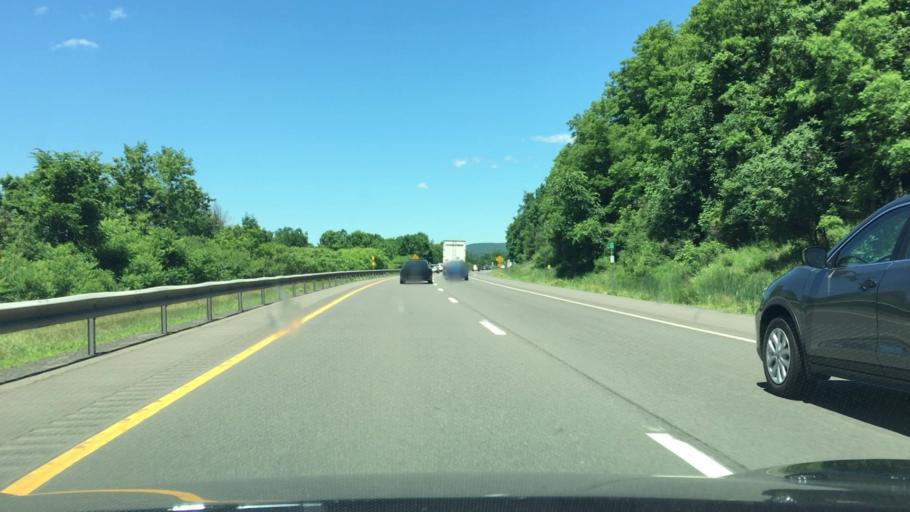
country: US
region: New York
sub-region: Cortland County
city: Homer
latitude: 42.6375
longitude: -76.1742
